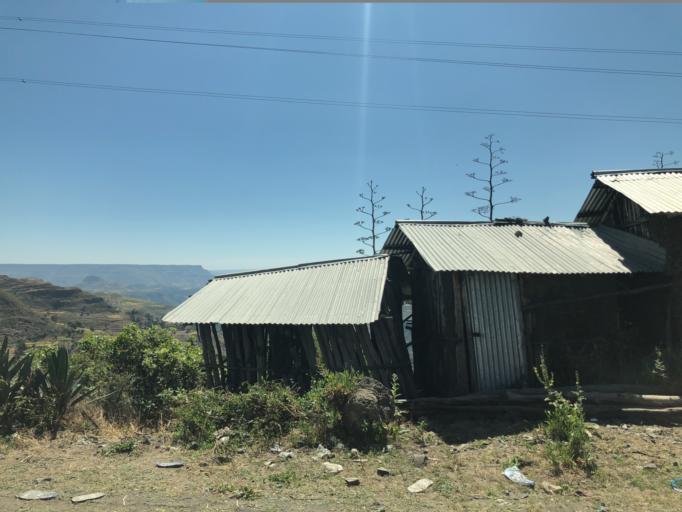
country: ET
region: Amhara
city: Lalibela
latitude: 11.8004
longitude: 38.5529
